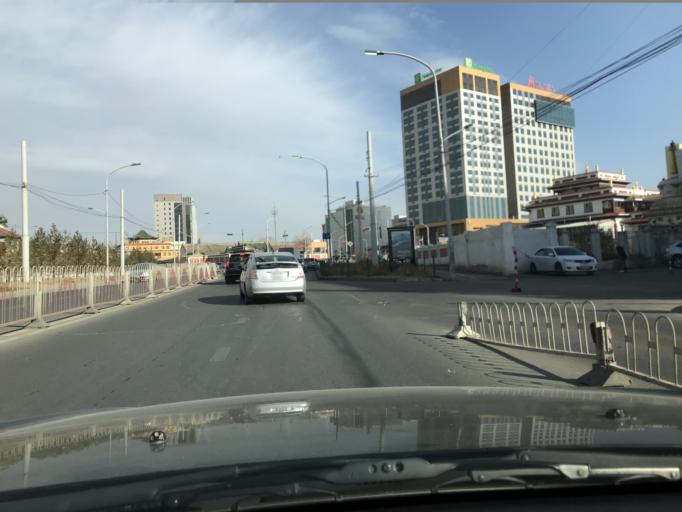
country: MN
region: Ulaanbaatar
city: Ulaanbaatar
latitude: 47.9203
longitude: 106.8994
